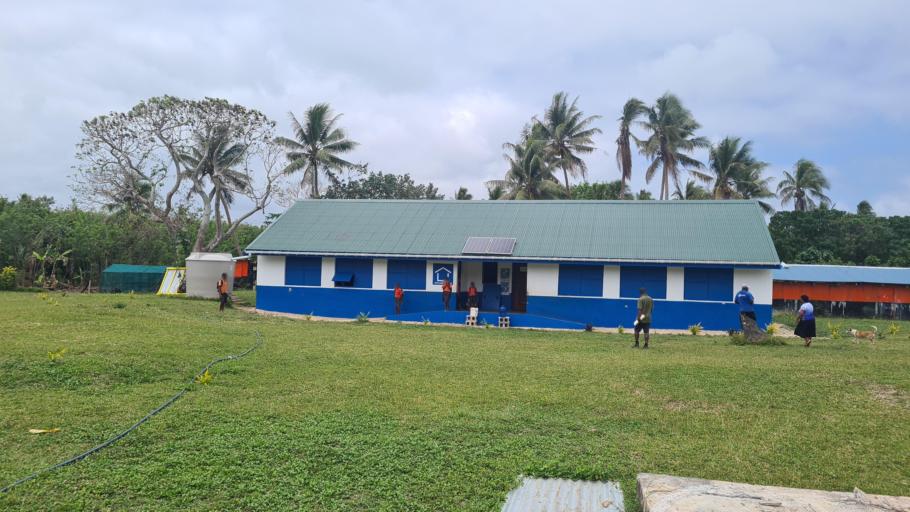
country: VU
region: Shefa
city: Port-Vila
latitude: -17.4994
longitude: 168.4073
